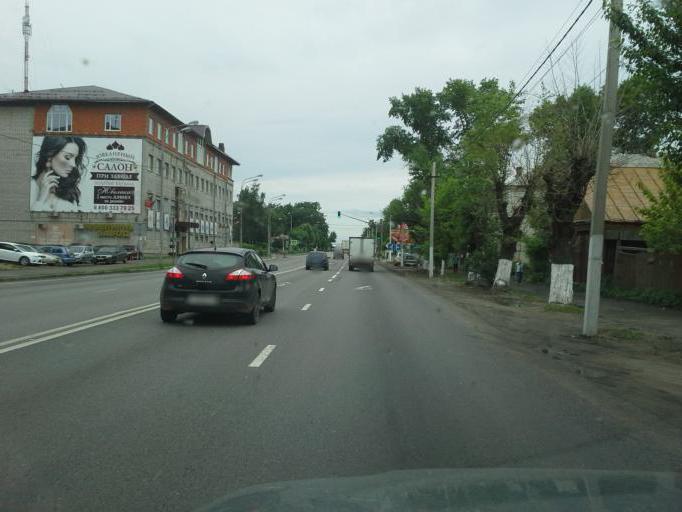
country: RU
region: Vladimir
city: Pokrov
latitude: 55.9176
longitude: 39.1730
